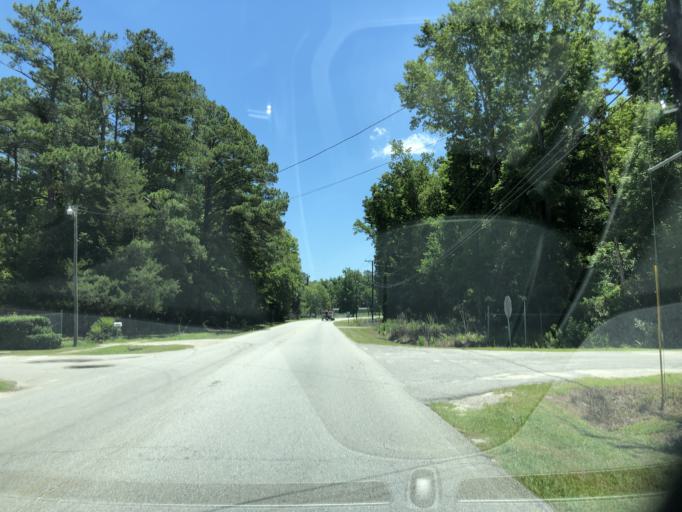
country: US
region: South Carolina
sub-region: Orangeburg County
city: Branchville
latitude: 33.2517
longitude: -80.8108
